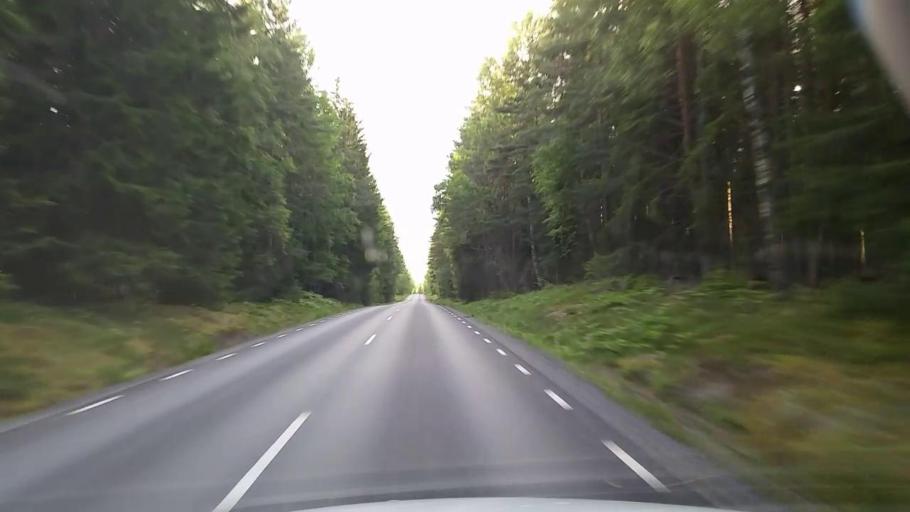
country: SE
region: Vaestmanland
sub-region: Kopings Kommun
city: Kolsva
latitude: 59.6832
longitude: 15.8394
